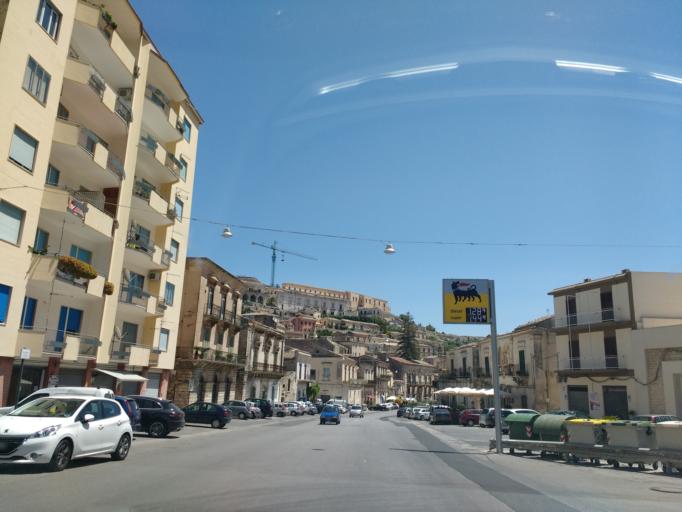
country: IT
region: Sicily
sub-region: Ragusa
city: Modica
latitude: 36.8648
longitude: 14.7586
